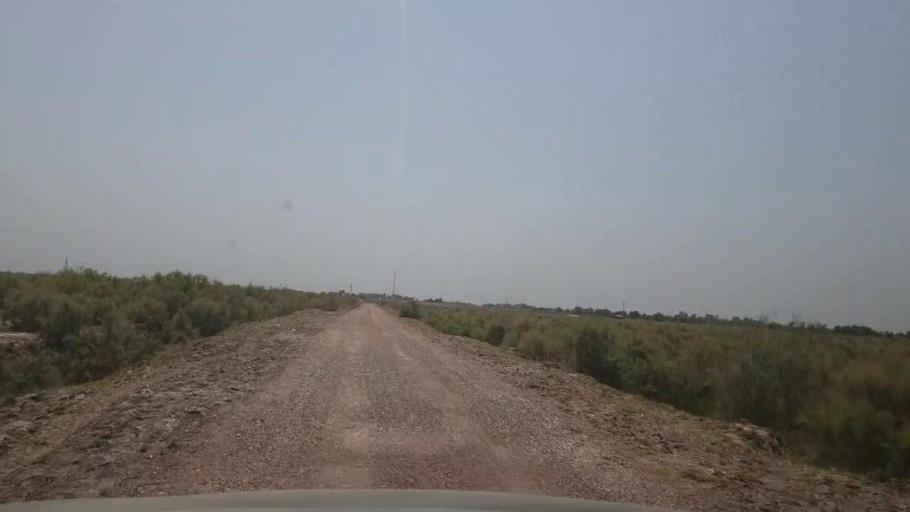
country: PK
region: Sindh
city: Lakhi
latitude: 27.8351
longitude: 68.6595
